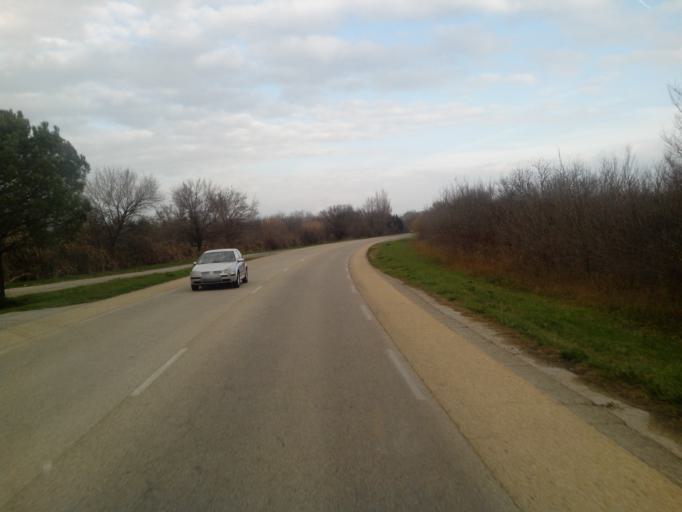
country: FR
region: Provence-Alpes-Cote d'Azur
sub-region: Departement des Bouches-du-Rhone
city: Saintes-Maries-de-la-Mer
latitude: 43.5511
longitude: 4.4038
